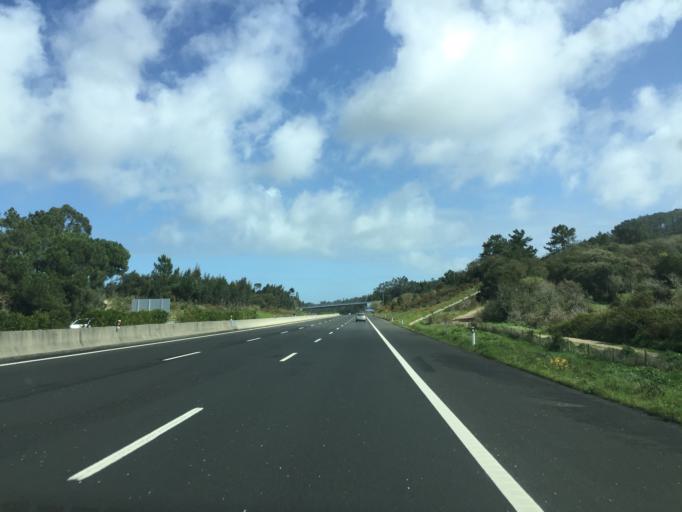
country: PT
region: Leiria
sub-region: Caldas da Rainha
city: Caldas da Rainha
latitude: 39.4673
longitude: -9.1118
